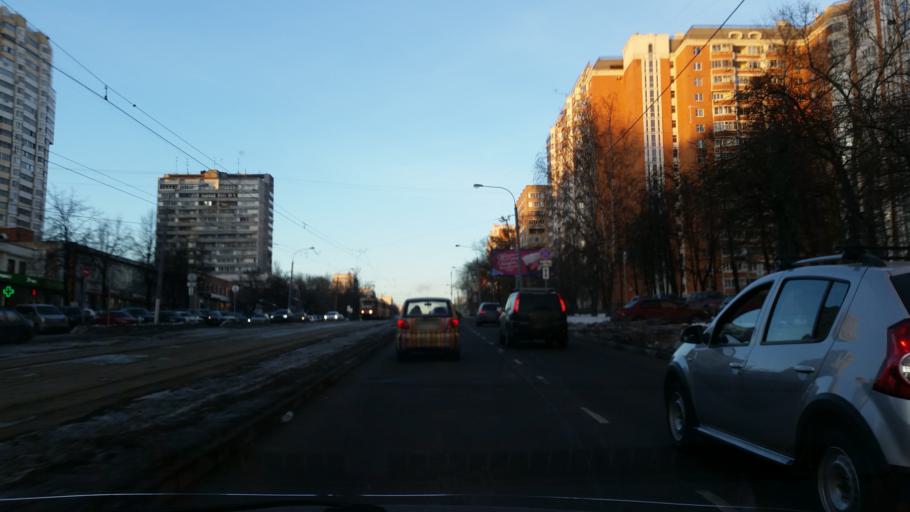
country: RU
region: Moscow
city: Nagornyy
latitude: 55.6464
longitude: 37.6057
